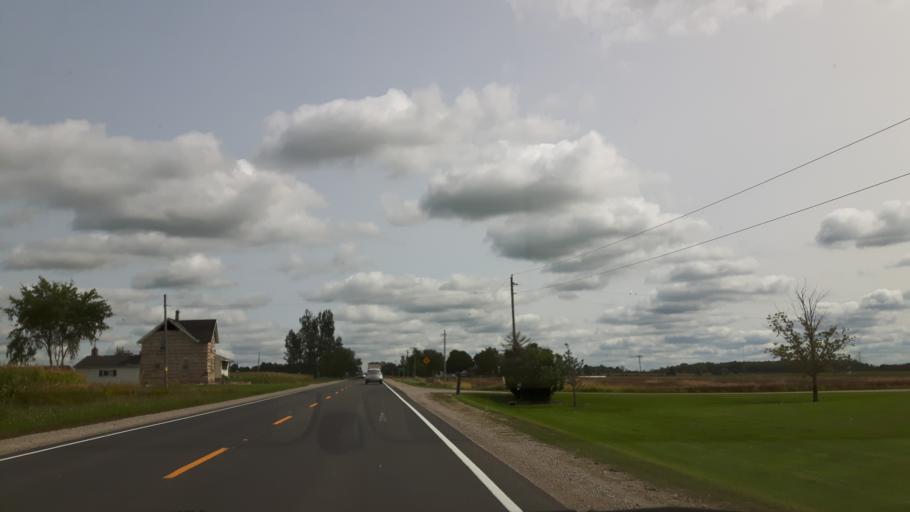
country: CA
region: Ontario
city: Huron East
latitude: 43.5737
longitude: -81.4398
